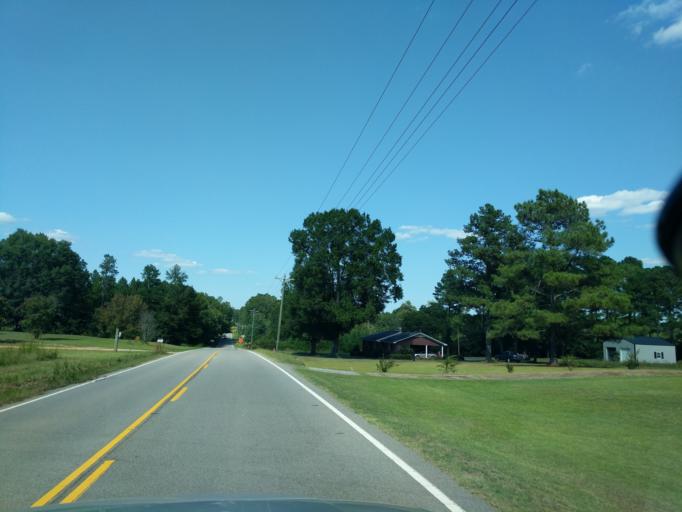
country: US
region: South Carolina
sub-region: Newberry County
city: Prosperity
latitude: 34.1418
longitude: -81.5350
